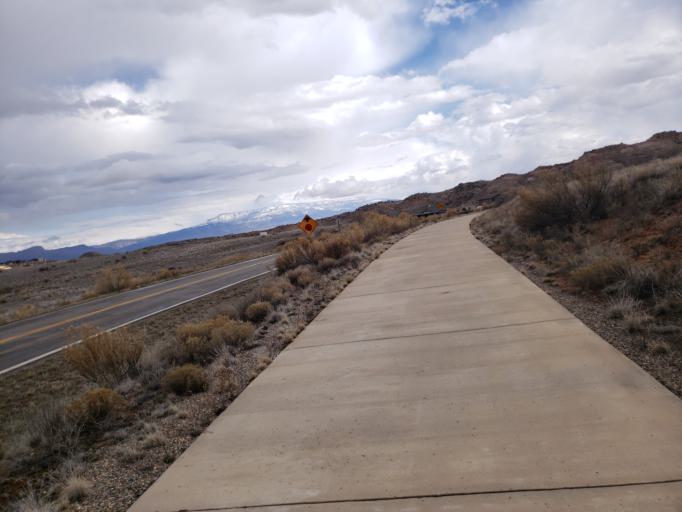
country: US
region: Colorado
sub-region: Mesa County
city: Redlands
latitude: 39.0437
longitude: -108.6269
